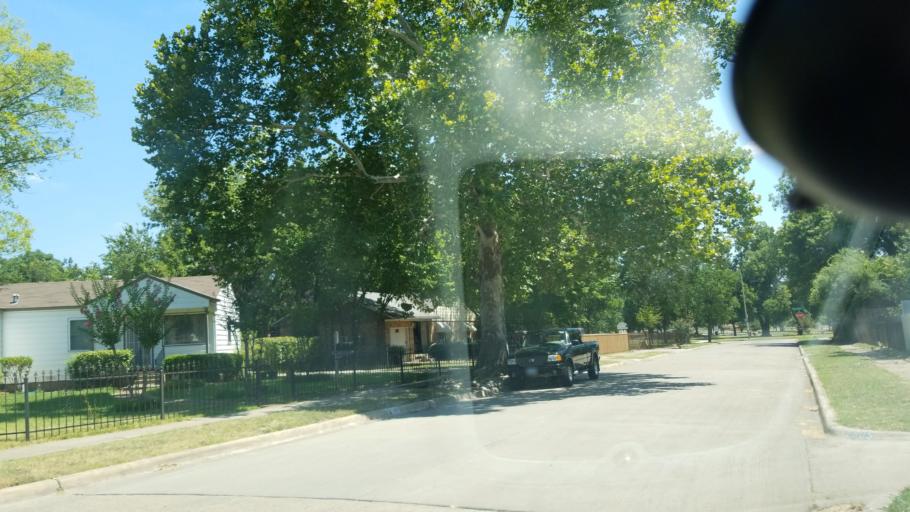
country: US
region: Texas
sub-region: Dallas County
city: Cockrell Hill
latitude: 32.7151
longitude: -96.8544
